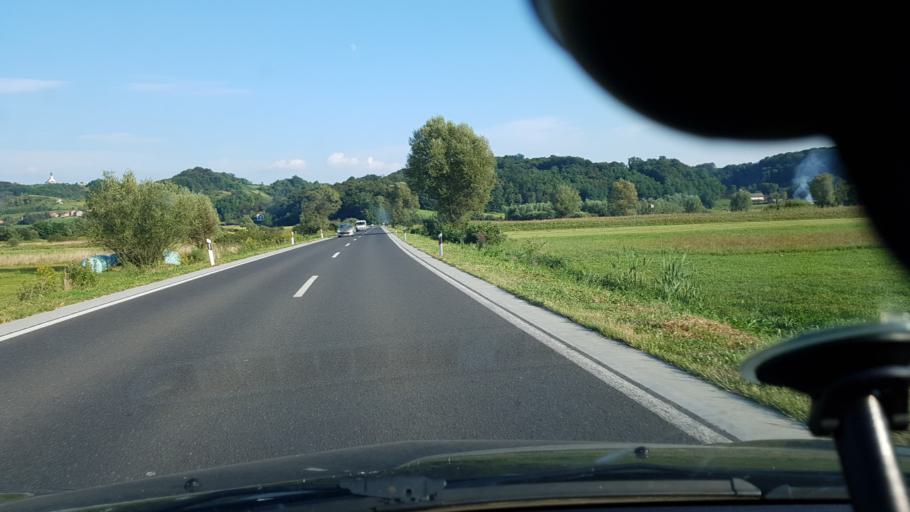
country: HR
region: Krapinsko-Zagorska
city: Zabok
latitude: 46.0336
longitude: 15.8290
